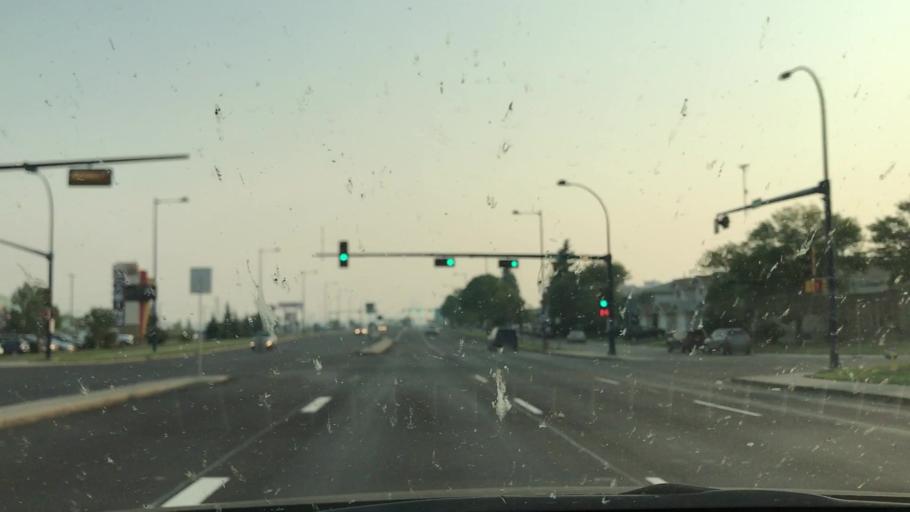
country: CA
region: Alberta
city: Edmonton
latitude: 53.5906
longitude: -113.4330
